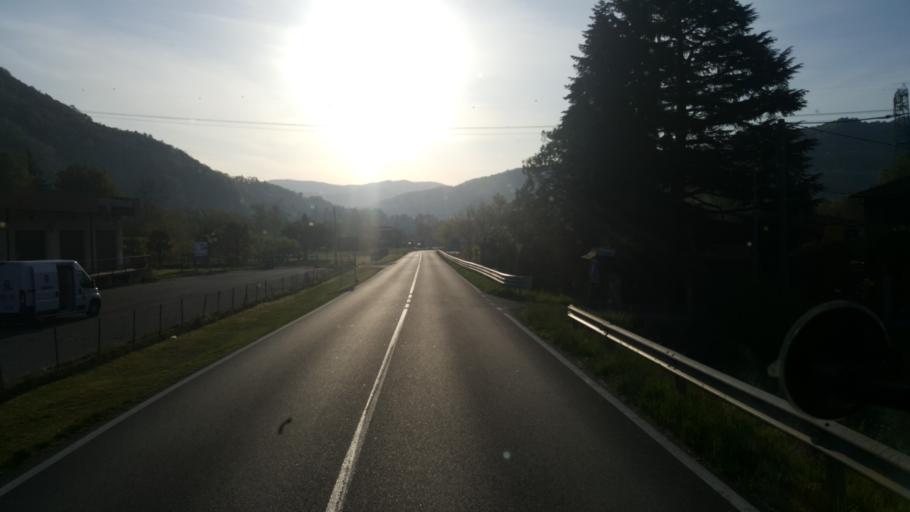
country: IT
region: Lombardy
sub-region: Provincia di Varese
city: Casalzuigno
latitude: 45.9068
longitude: 8.7180
